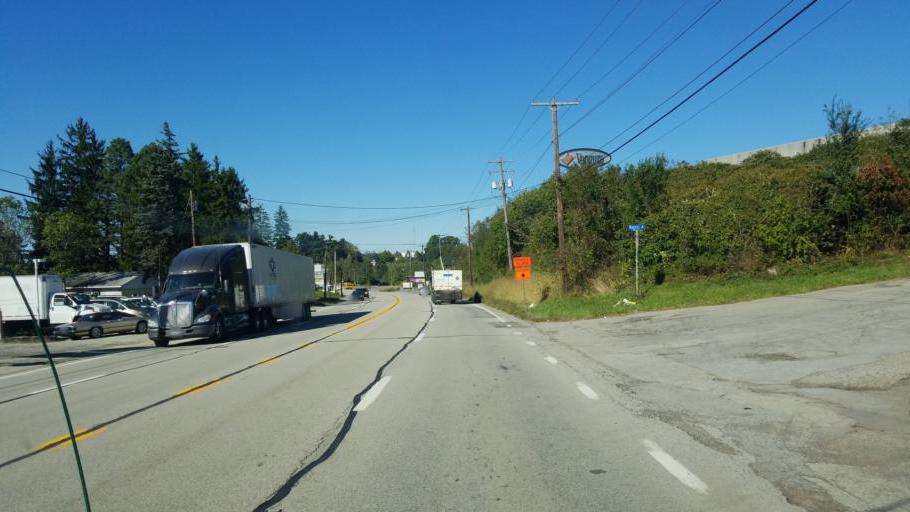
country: US
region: Pennsylvania
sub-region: Westmoreland County
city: Trafford
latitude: 40.3529
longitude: -79.7682
